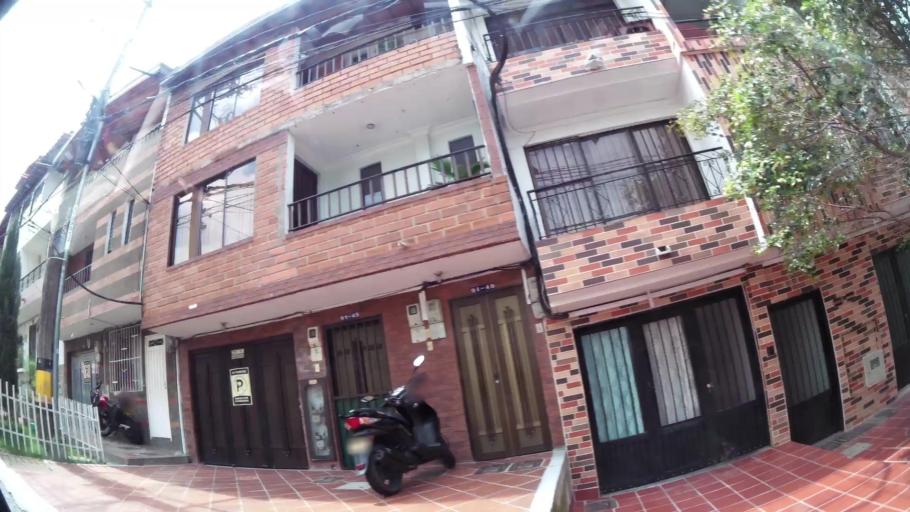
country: CO
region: Antioquia
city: Medellin
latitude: 6.2552
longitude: -75.6085
